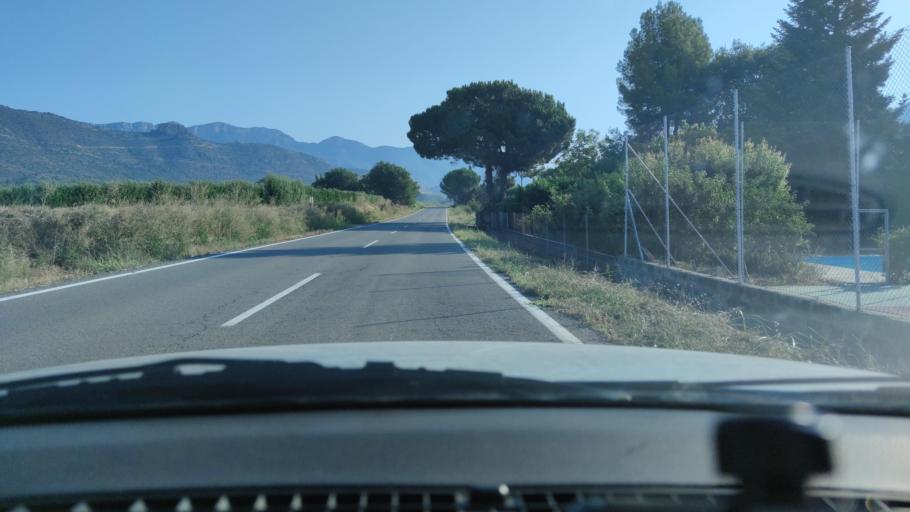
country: ES
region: Catalonia
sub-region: Provincia de Lleida
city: Camarasa
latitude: 41.8486
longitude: 0.8259
